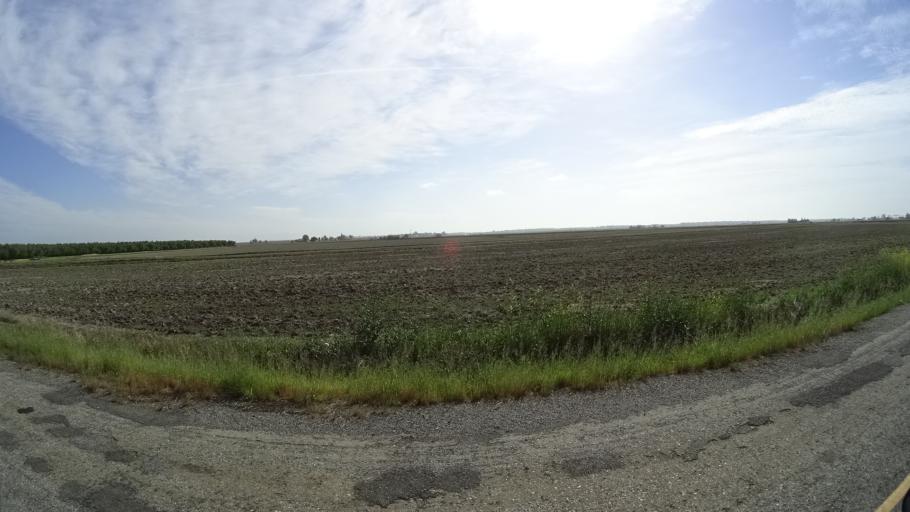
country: US
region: California
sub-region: Glenn County
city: Hamilton City
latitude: 39.6074
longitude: -122.0463
